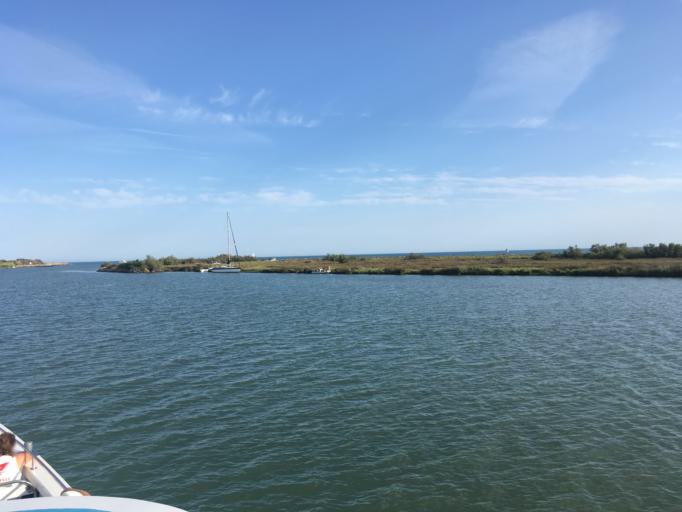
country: FR
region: Provence-Alpes-Cote d'Azur
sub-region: Departement des Bouches-du-Rhone
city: Saintes-Maries-de-la-Mer
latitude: 43.4551
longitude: 4.3931
